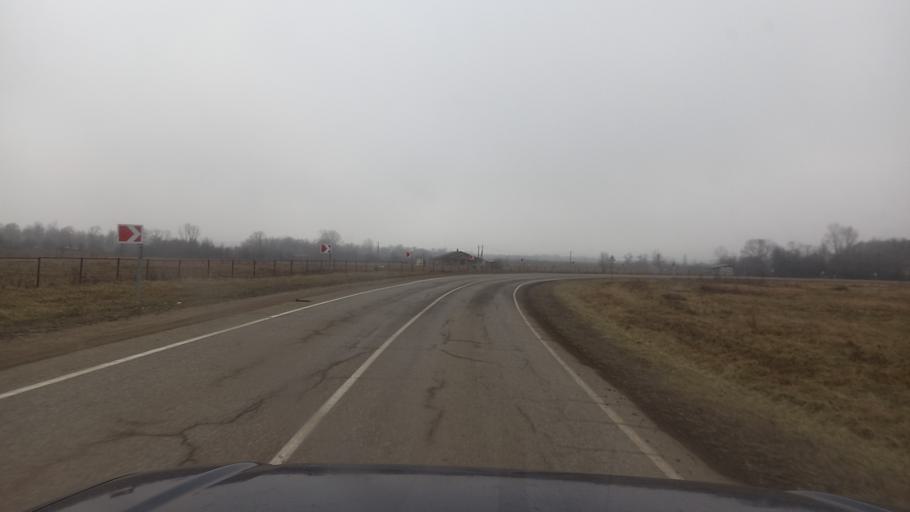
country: RU
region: Krasnodarskiy
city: Neftegorsk
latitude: 44.2883
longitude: 39.8220
